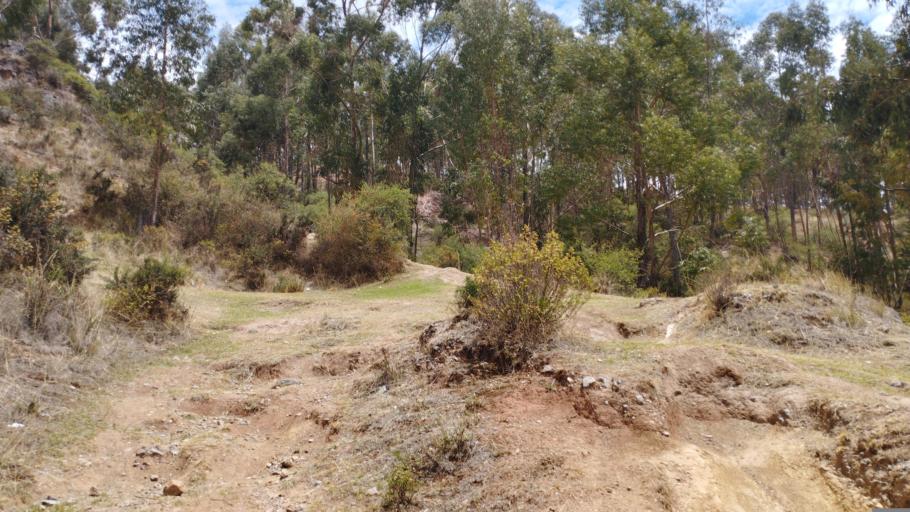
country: PE
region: Cusco
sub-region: Provincia de Cusco
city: Cusco
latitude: -13.5193
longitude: -71.9443
